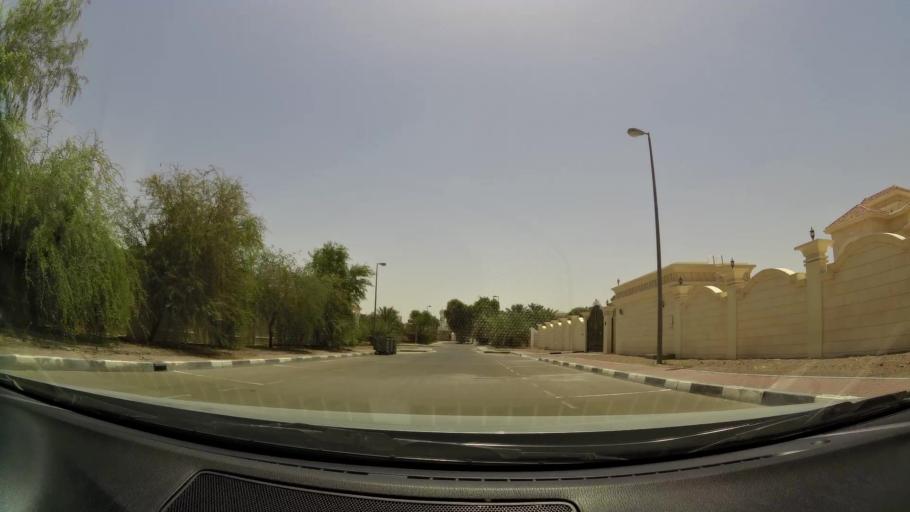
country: OM
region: Al Buraimi
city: Al Buraymi
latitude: 24.2825
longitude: 55.7574
